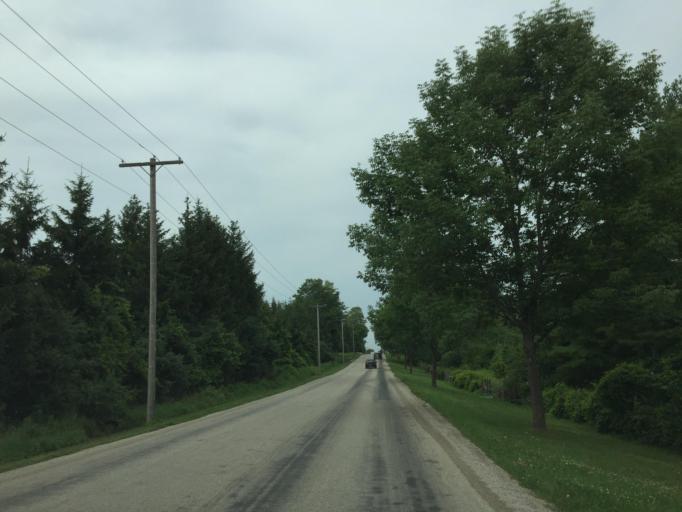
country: CA
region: Ontario
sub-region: Wellington County
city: Guelph
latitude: 43.6040
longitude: -80.2593
